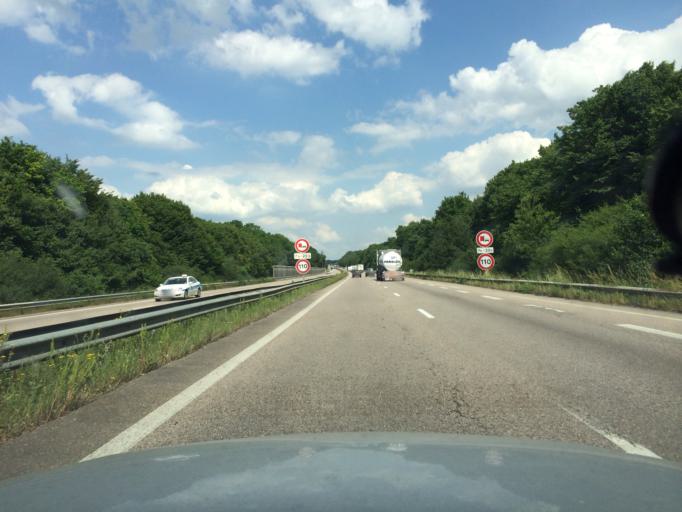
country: FR
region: Lorraine
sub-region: Departement de Meurthe-et-Moselle
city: Velaine-en-Haye
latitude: 48.6888
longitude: 6.0161
